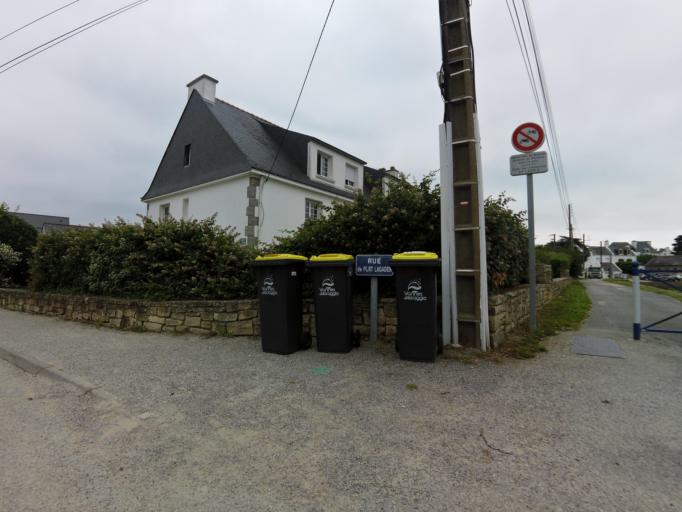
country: FR
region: Brittany
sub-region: Departement du Morbihan
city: Larmor-Baden
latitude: 47.5849
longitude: -2.9001
